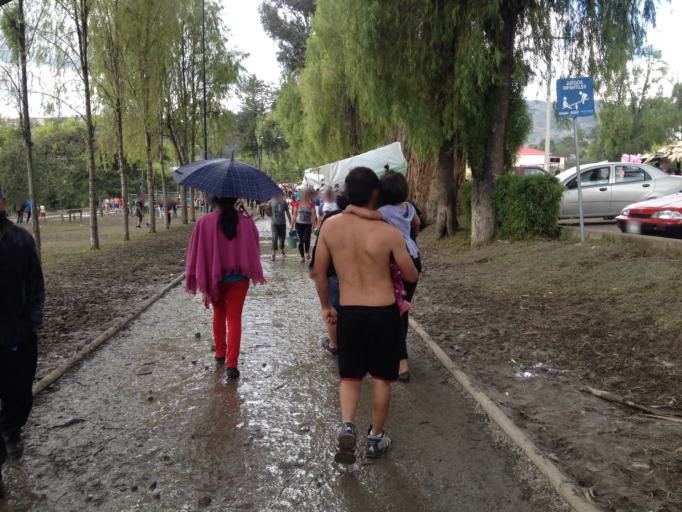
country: EC
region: Azuay
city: Gualaceo
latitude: -2.8919
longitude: -78.7739
